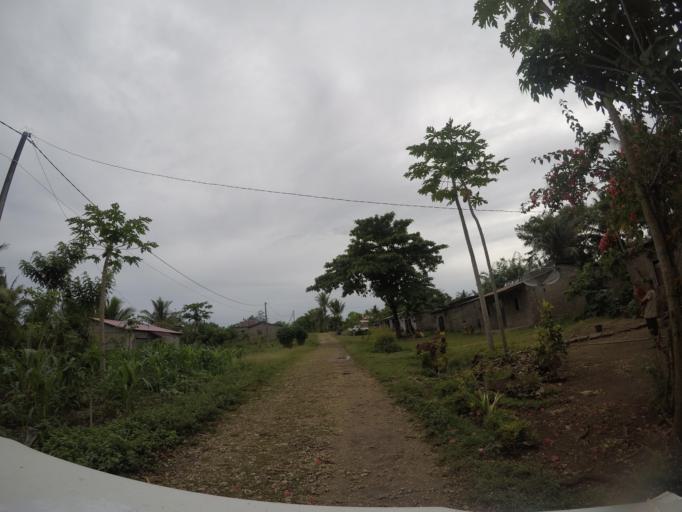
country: TL
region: Lautem
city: Lospalos
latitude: -8.5311
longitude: 127.0026
